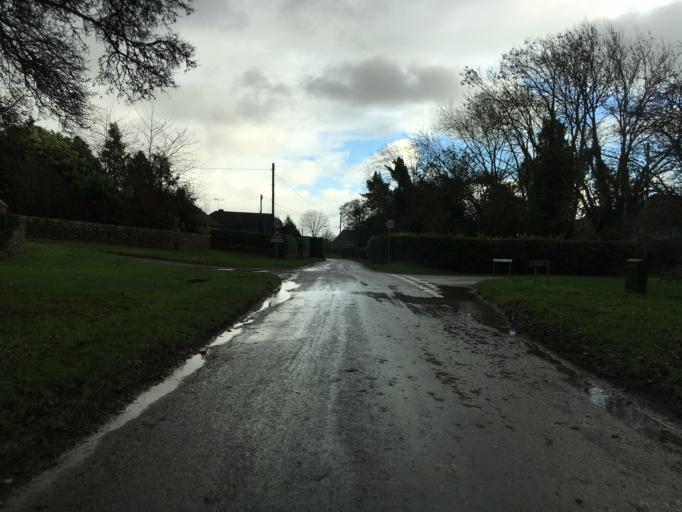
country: GB
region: England
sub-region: Wiltshire
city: Hankerton
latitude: 51.6338
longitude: -2.0798
